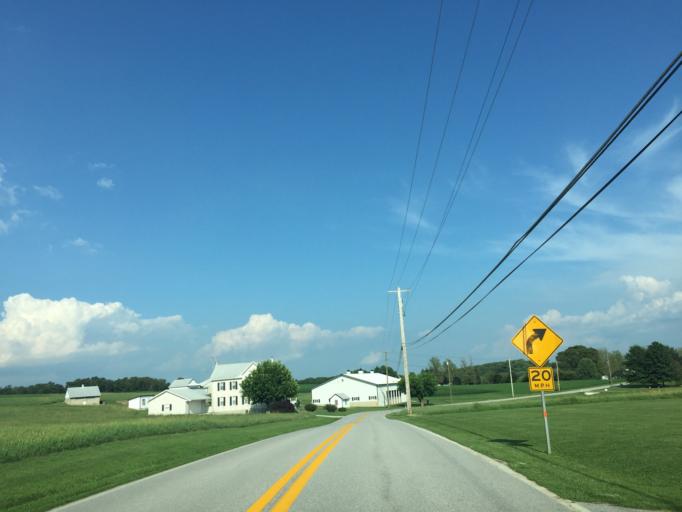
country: US
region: Maryland
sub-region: Carroll County
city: Manchester
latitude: 39.6528
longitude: -76.8525
